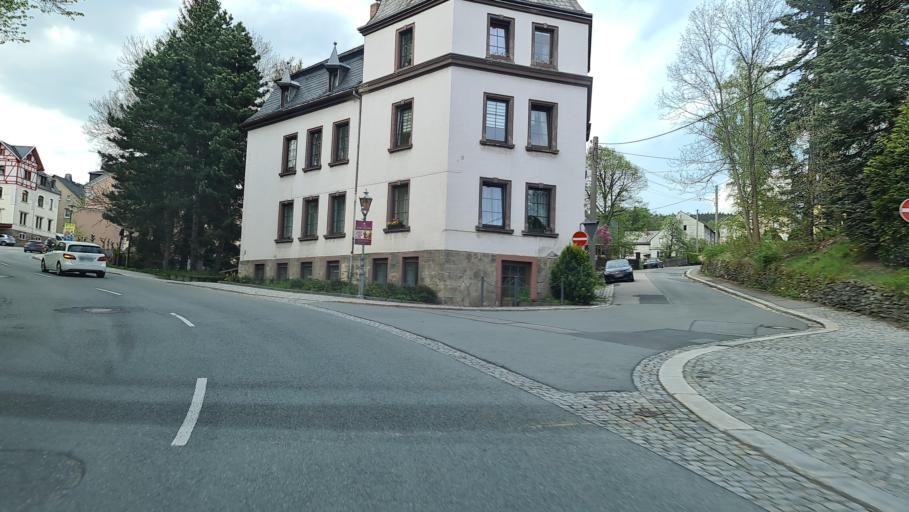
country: DE
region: Saxony
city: Beierfeld
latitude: 50.5655
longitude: 12.7915
